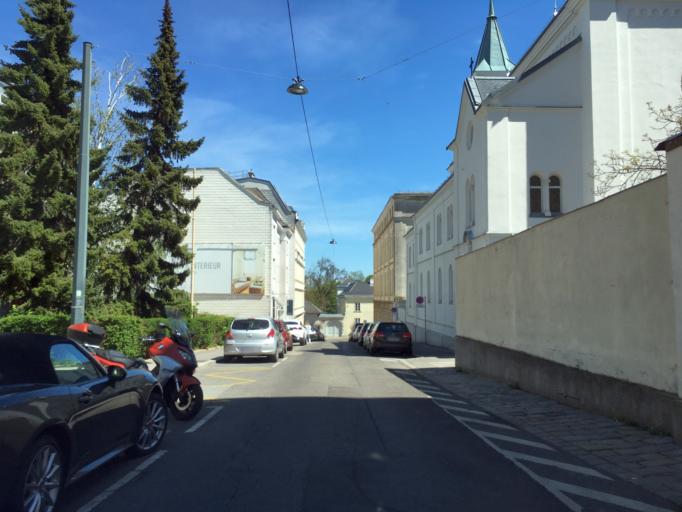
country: AT
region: Vienna
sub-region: Wien Stadt
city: Vienna
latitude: 48.2427
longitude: 16.3540
